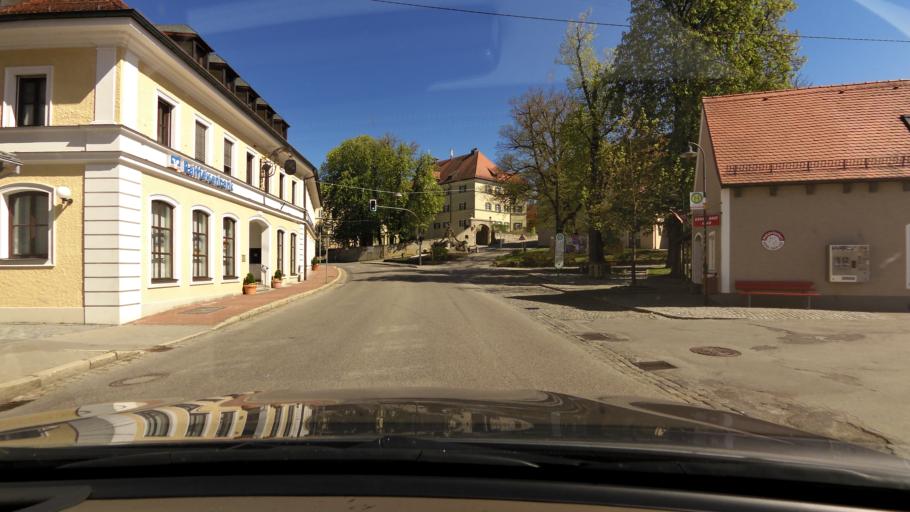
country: DE
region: Bavaria
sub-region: Upper Bavaria
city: Haag in Oberbayern
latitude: 48.1617
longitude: 12.1820
